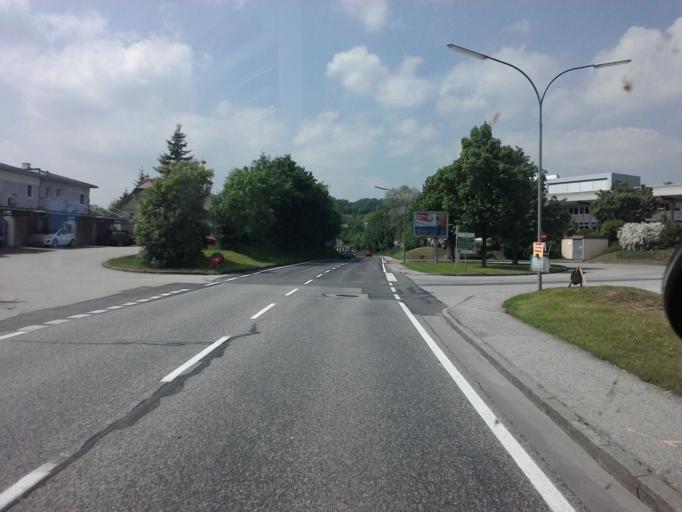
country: AT
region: Upper Austria
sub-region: Politischer Bezirk Steyr-Land
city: Garsten
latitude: 48.0443
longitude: 14.3796
